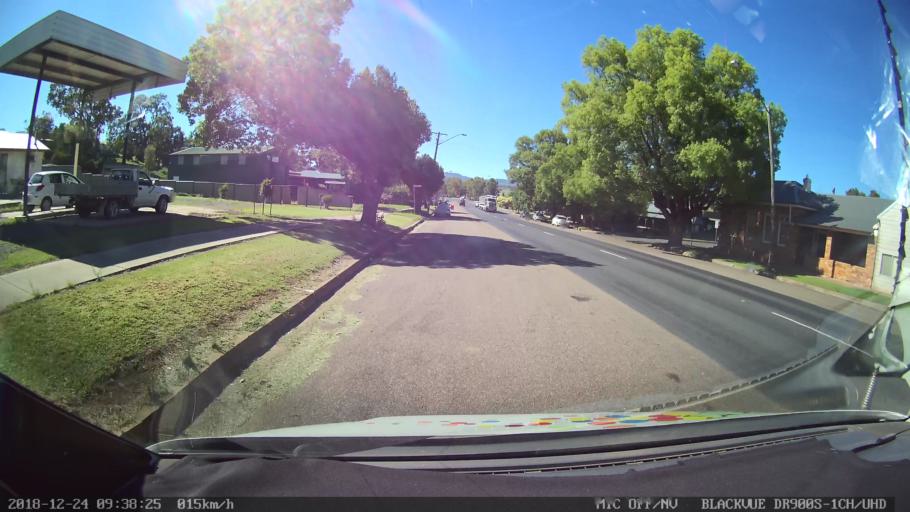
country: AU
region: New South Wales
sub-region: Liverpool Plains
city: Quirindi
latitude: -31.6474
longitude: 150.7261
